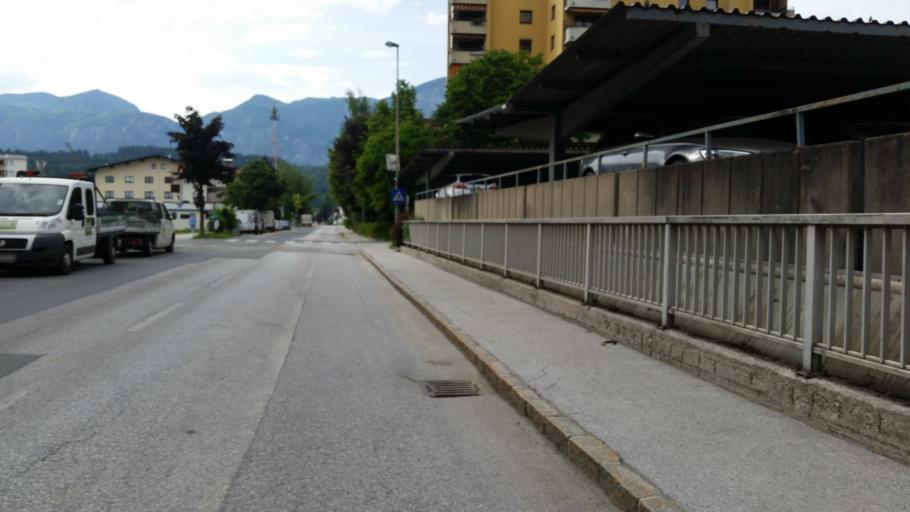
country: AT
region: Tyrol
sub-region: Politischer Bezirk Kufstein
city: Worgl
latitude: 47.4899
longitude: 12.0702
